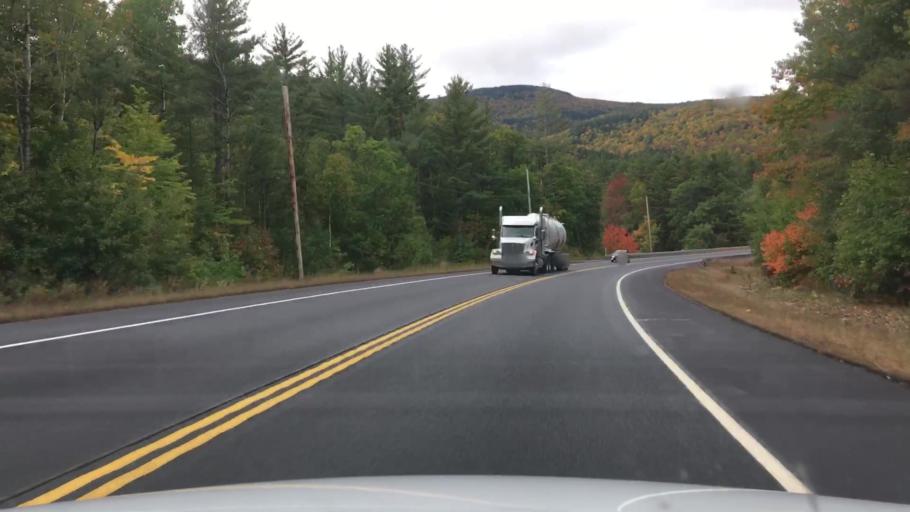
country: US
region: Maine
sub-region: Oxford County
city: Bethel
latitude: 44.4010
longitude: -70.9280
